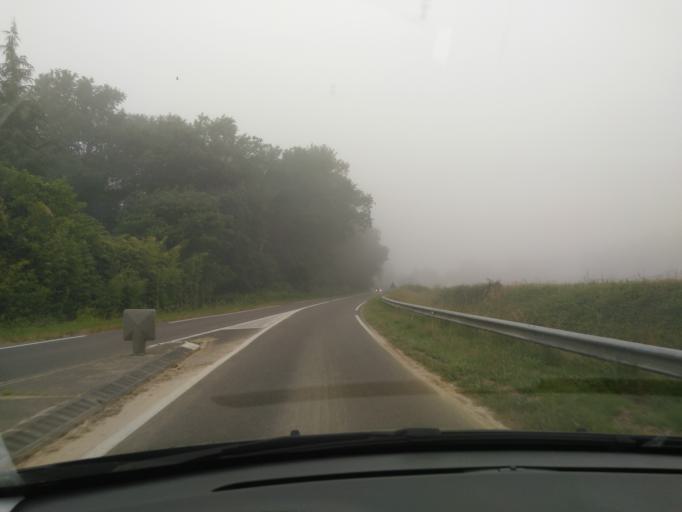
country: FR
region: Aquitaine
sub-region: Departement des Landes
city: Villeneuve-de-Marsan
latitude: 43.8819
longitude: -0.3500
